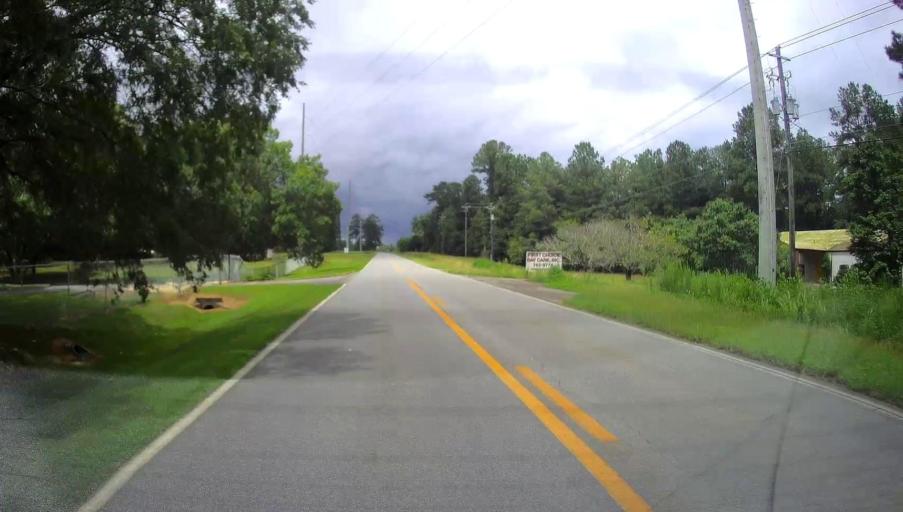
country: US
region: Georgia
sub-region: Bibb County
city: Macon
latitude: 32.8079
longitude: -83.5390
